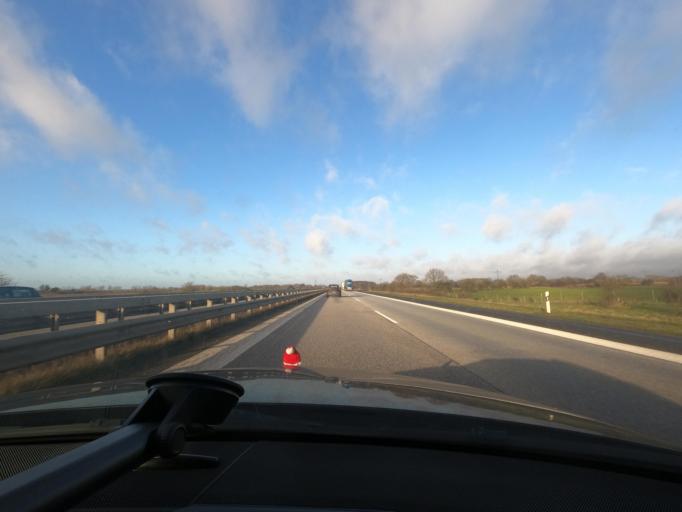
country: DE
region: Schleswig-Holstein
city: Lottorf
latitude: 54.4329
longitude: 9.5954
